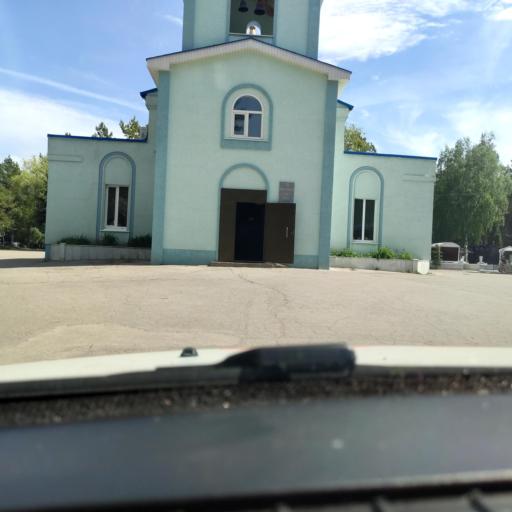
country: RU
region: Samara
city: Samara
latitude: 53.1159
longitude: 50.2323
